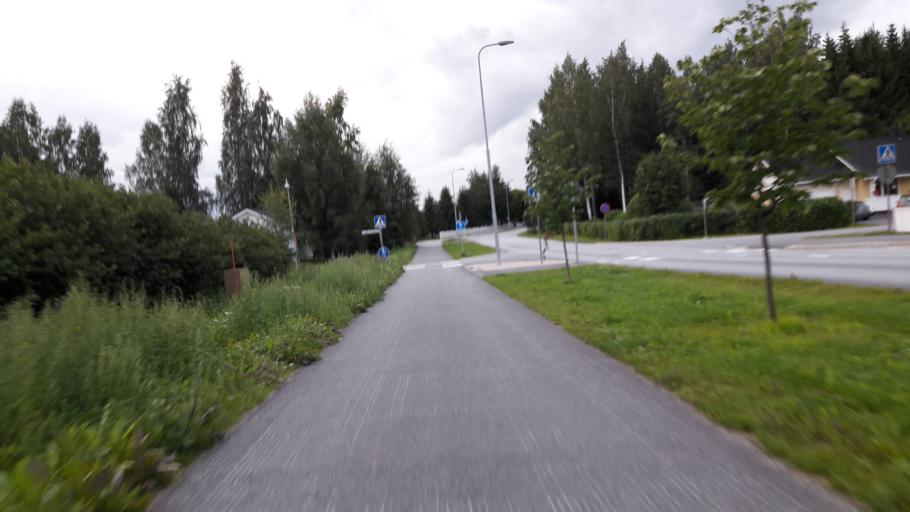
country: FI
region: North Karelia
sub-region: Joensuu
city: Joensuu
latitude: 62.5293
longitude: 29.8434
